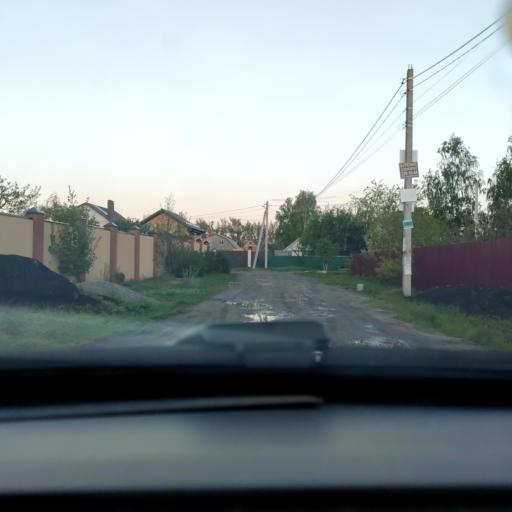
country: RU
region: Voronezj
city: Novaya Usman'
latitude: 51.6542
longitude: 39.4259
